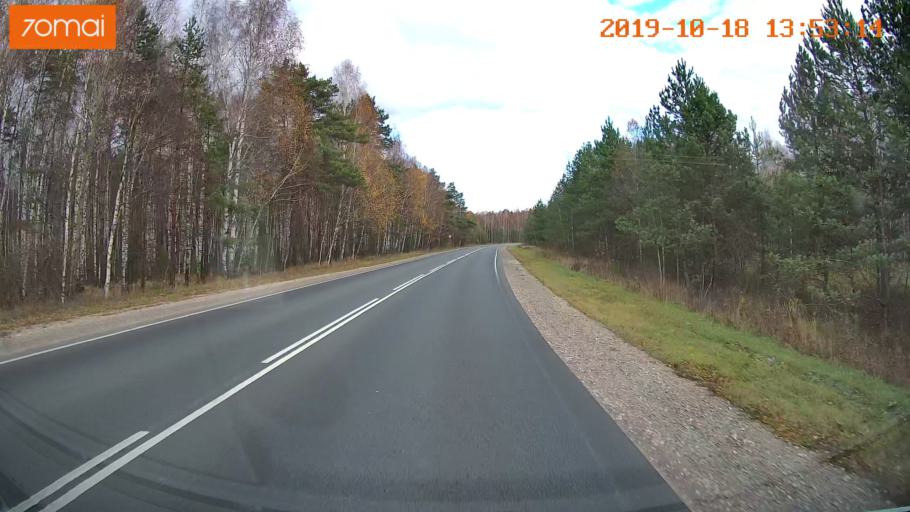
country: RU
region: Moskovskaya
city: Radovitskiy
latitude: 55.0369
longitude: 39.9773
